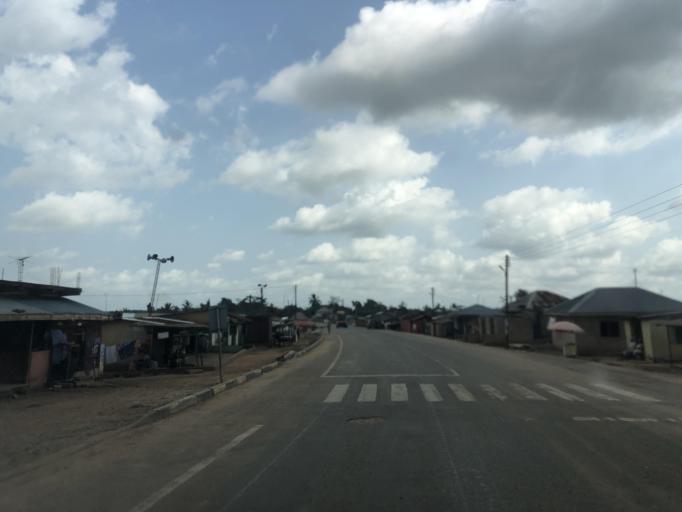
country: GH
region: Central
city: Elmina
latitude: 5.2338
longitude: -1.3292
